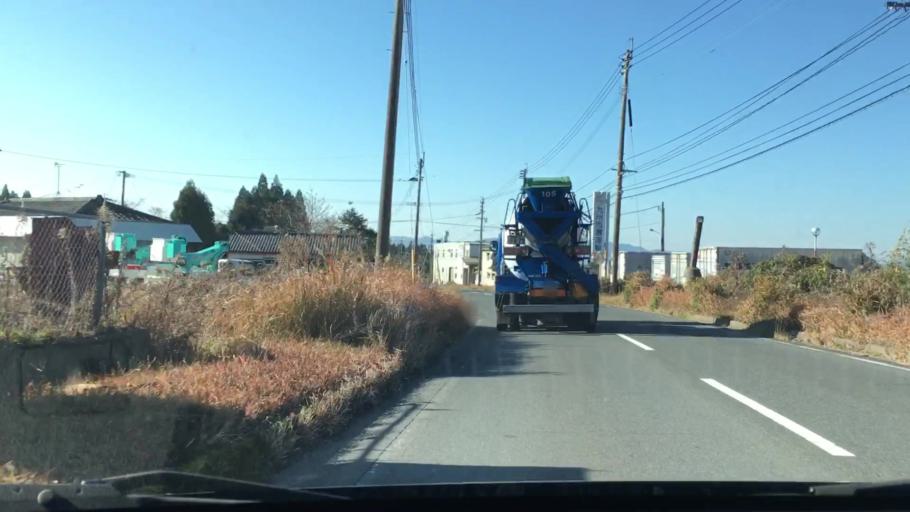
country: JP
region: Kagoshima
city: Kajiki
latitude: 31.7707
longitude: 130.6940
